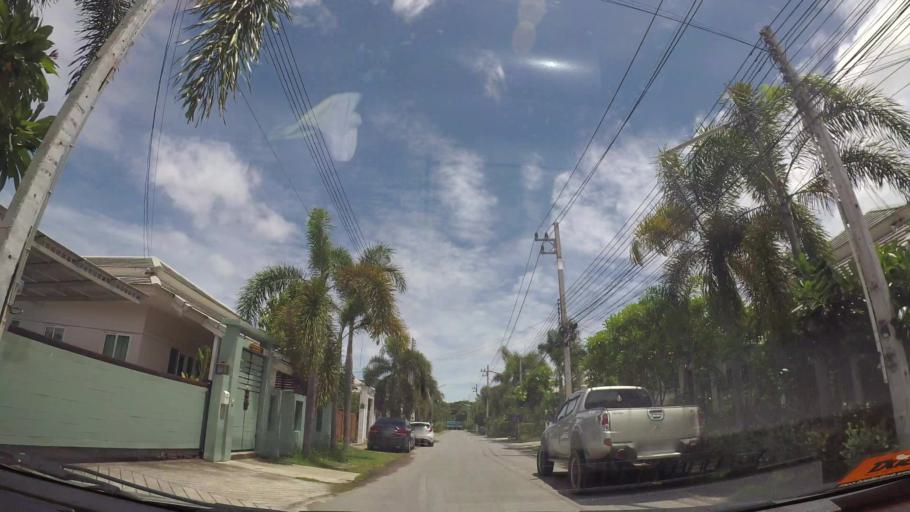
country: TH
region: Chon Buri
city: Sattahip
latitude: 12.7420
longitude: 100.8915
